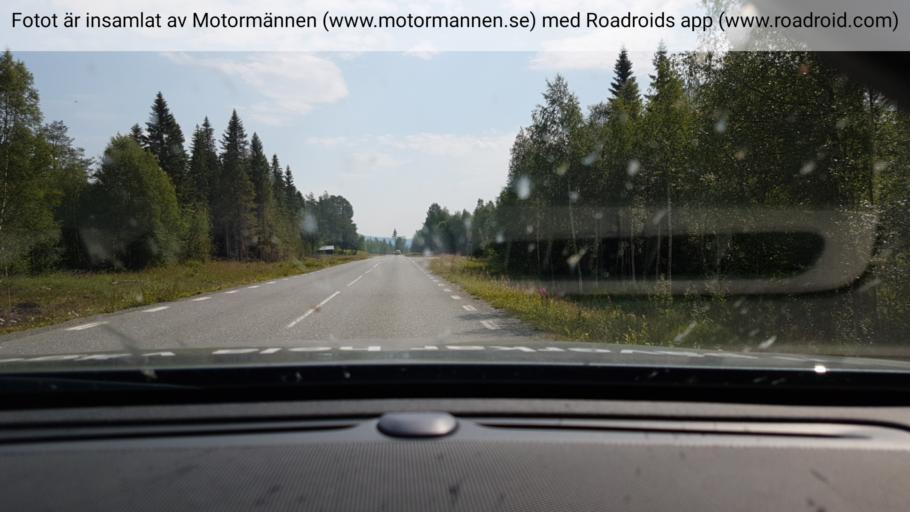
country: SE
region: Vaesterbotten
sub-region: Vilhelmina Kommun
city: Sjoberg
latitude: 65.4758
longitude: 16.0102
